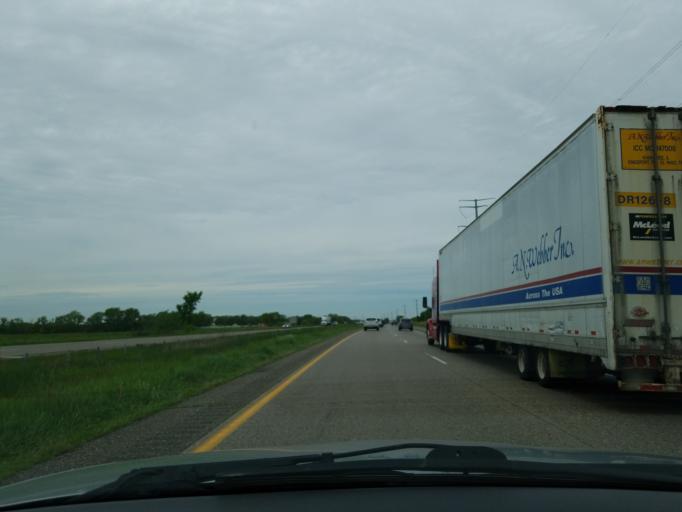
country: US
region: Minnesota
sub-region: Sherburne County
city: Becker
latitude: 45.3564
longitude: -93.9323
